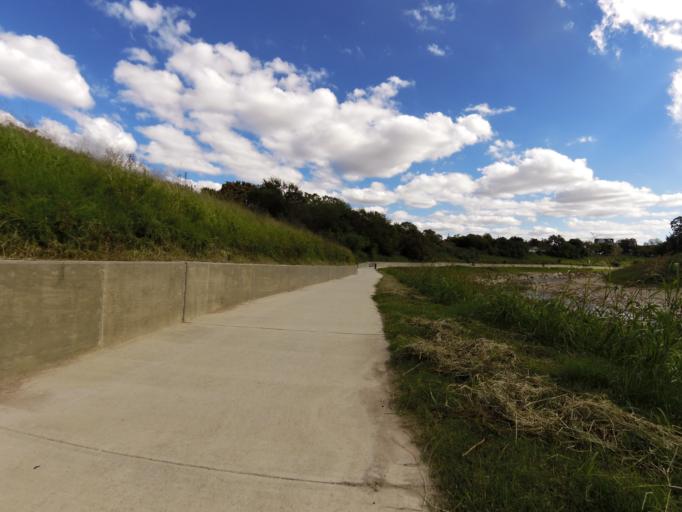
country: US
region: Texas
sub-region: Bexar County
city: San Antonio
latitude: 29.3993
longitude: -98.5027
